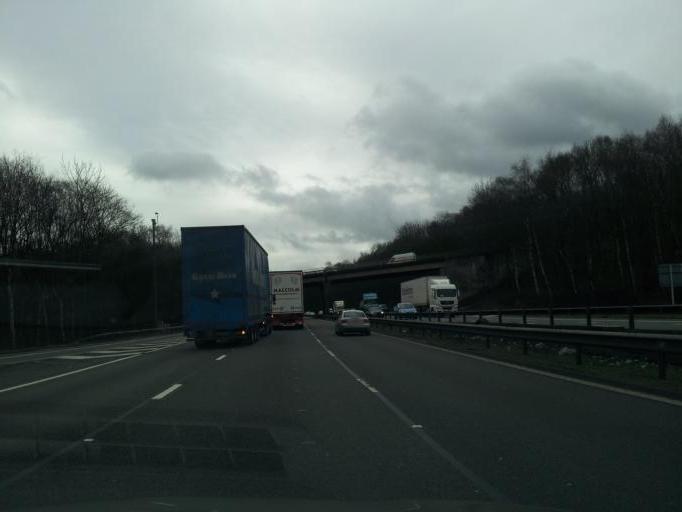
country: GB
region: England
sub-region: Staffordshire
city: Newcastle under Lyme
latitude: 52.9748
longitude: -2.2264
